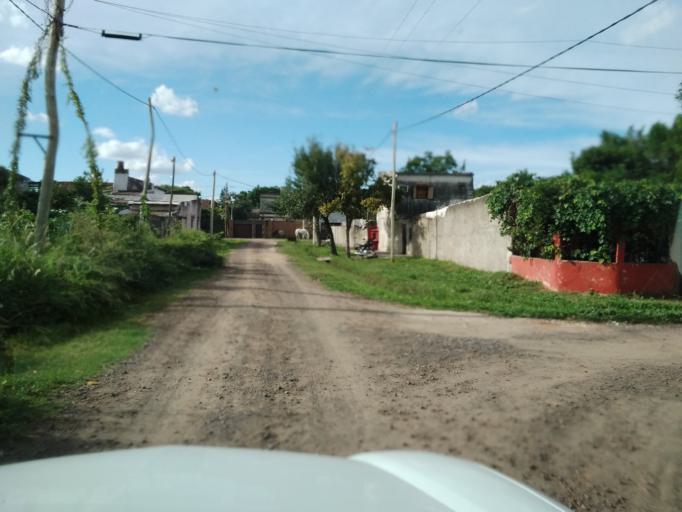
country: AR
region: Corrientes
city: Corrientes
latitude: -27.4876
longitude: -58.8424
